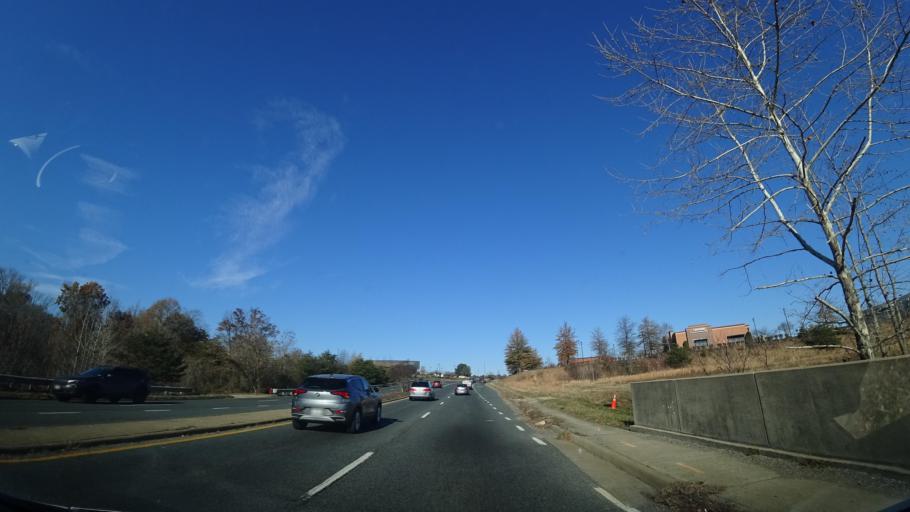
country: US
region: Virginia
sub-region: City of Fredericksburg
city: Fredericksburg
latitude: 38.2344
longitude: -77.5054
